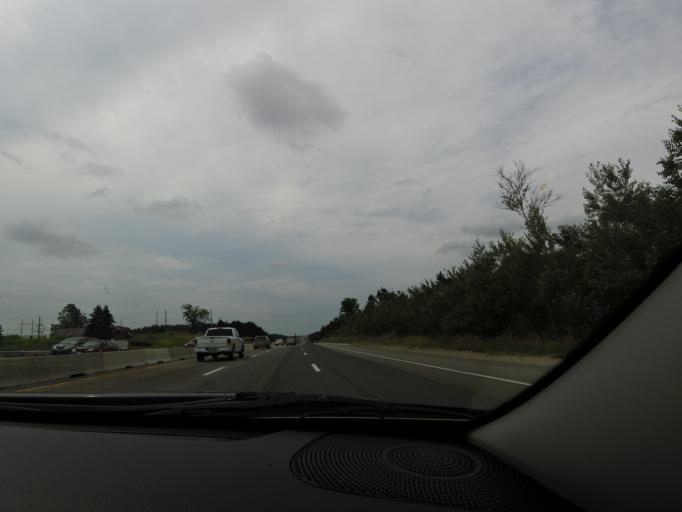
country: CA
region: Ontario
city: Innisfil
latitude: 44.3258
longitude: -79.6828
